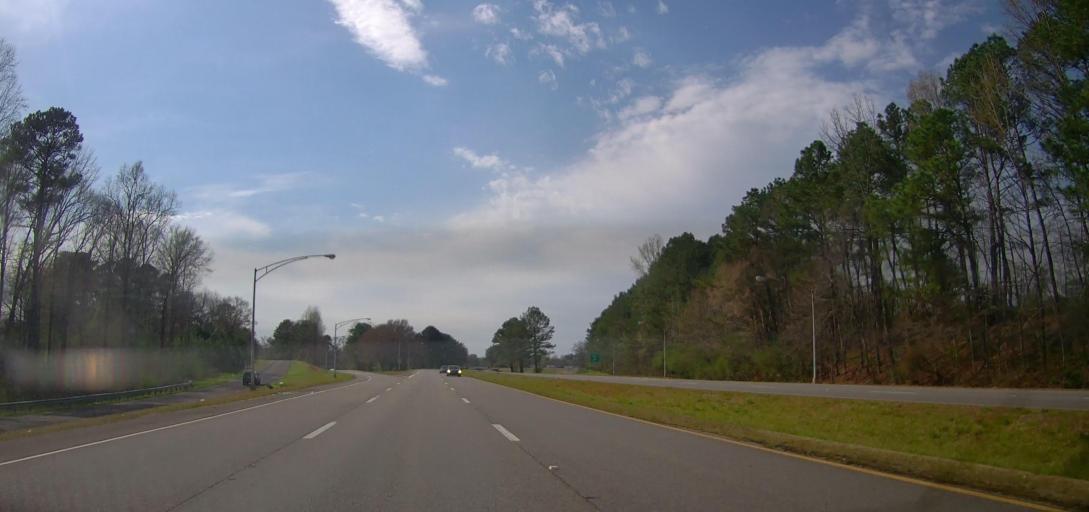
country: US
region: Alabama
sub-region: Jefferson County
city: Adamsville
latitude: 33.5840
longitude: -86.9281
